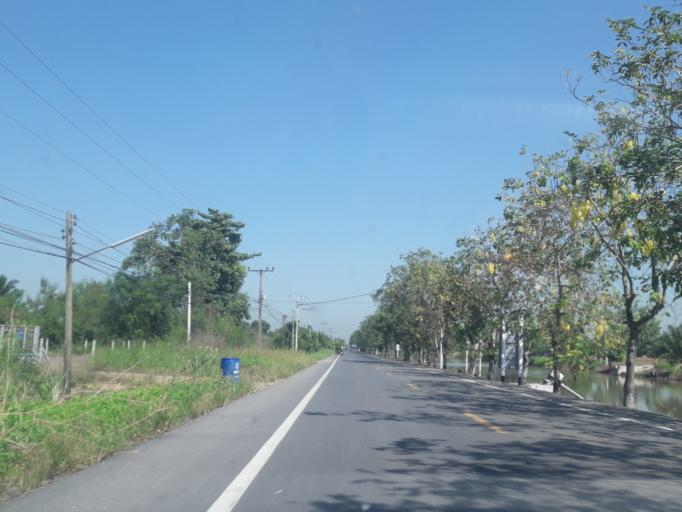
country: TH
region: Pathum Thani
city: Nong Suea
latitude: 14.1591
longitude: 100.8459
